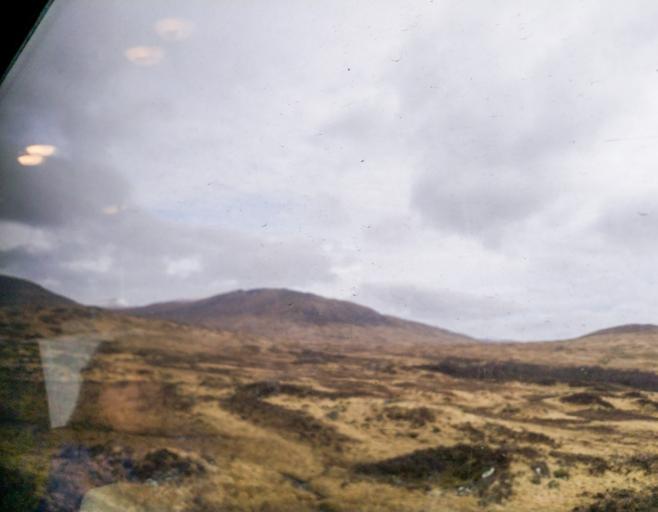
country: GB
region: Scotland
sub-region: Highland
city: Spean Bridge
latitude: 56.6943
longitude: -4.5733
